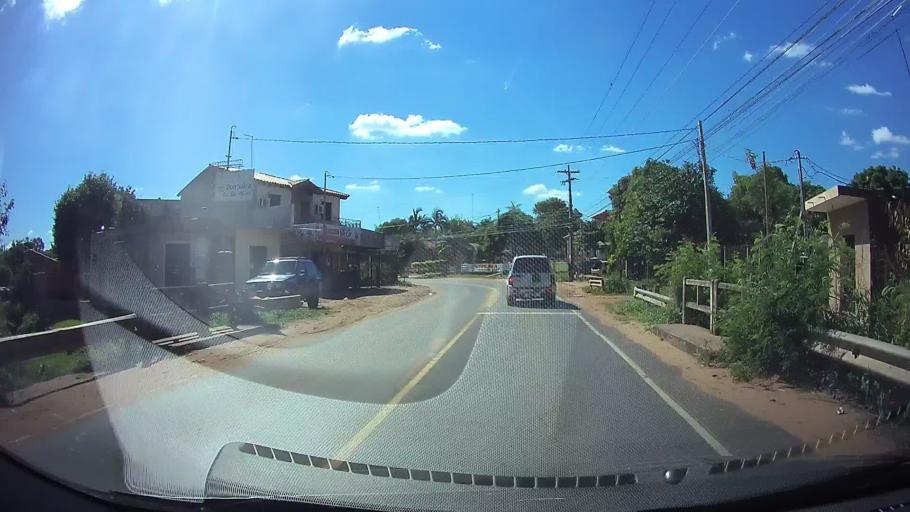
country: PY
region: Central
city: Limpio
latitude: -25.2062
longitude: -57.4626
